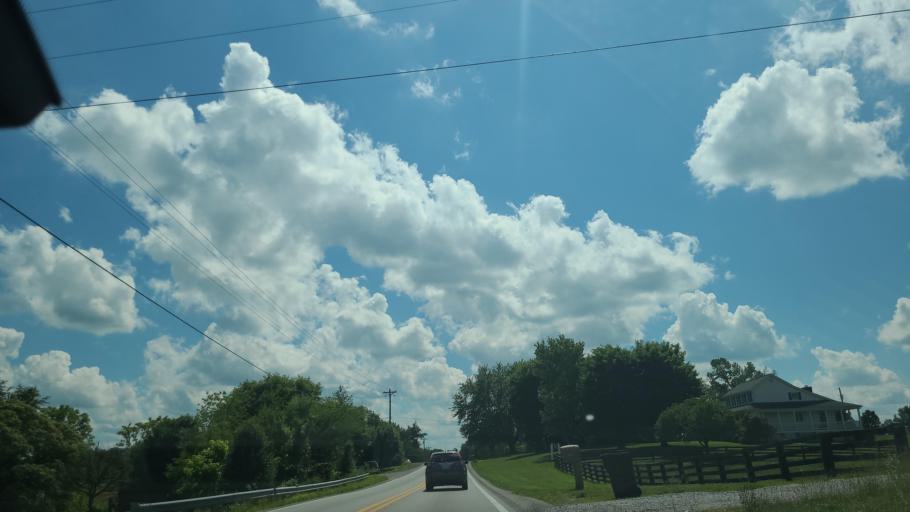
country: US
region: Kentucky
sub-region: Whitley County
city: Corbin
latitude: 36.9080
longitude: -84.1558
